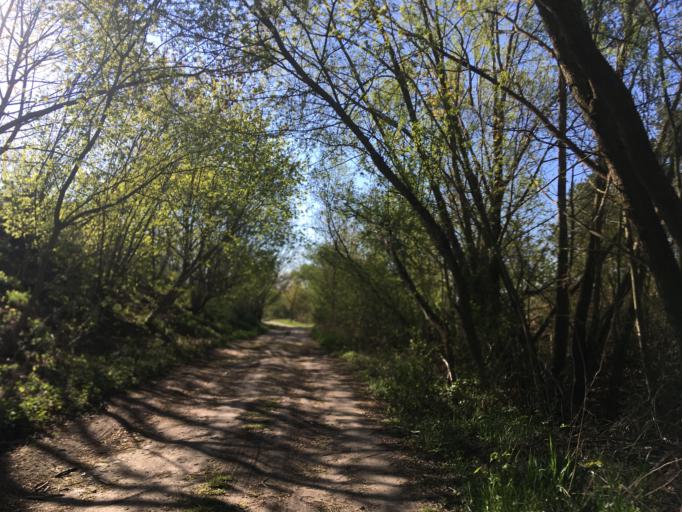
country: DE
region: Berlin
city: Stadtrandsiedlung Malchow
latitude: 52.5852
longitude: 13.4886
